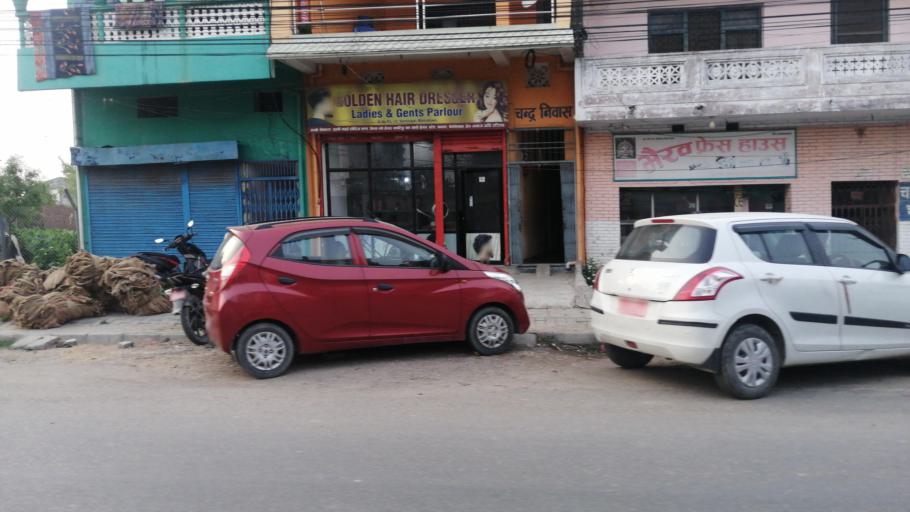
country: NP
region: Western Region
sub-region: Lumbini Zone
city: Bhairahawa
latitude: 27.5058
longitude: 83.4581
